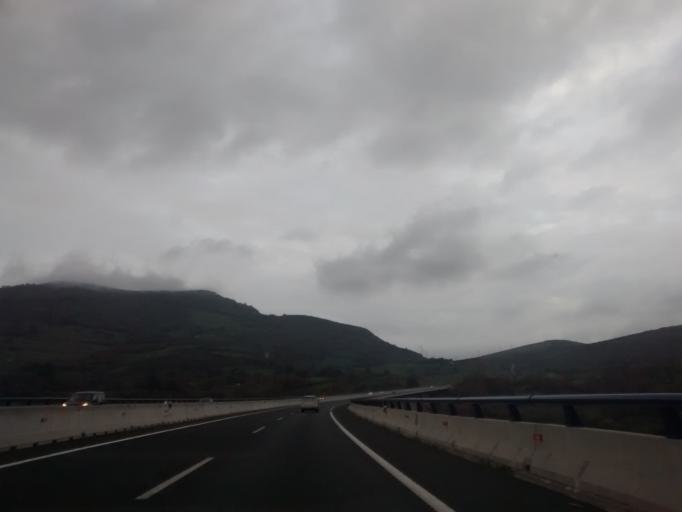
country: ES
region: Cantabria
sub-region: Provincia de Cantabria
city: Arenas de Iguna
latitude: 43.1908
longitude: -4.0682
